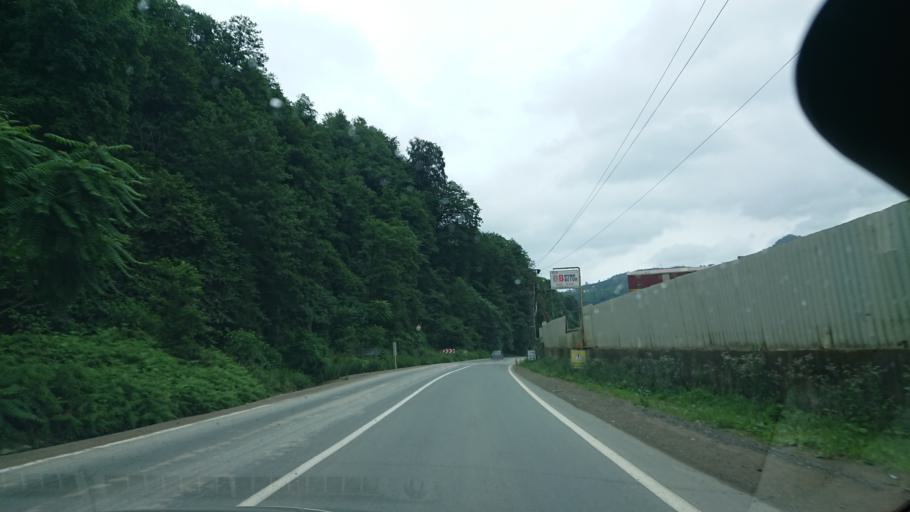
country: TR
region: Rize
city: Gundogdu
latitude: 41.0160
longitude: 40.5684
